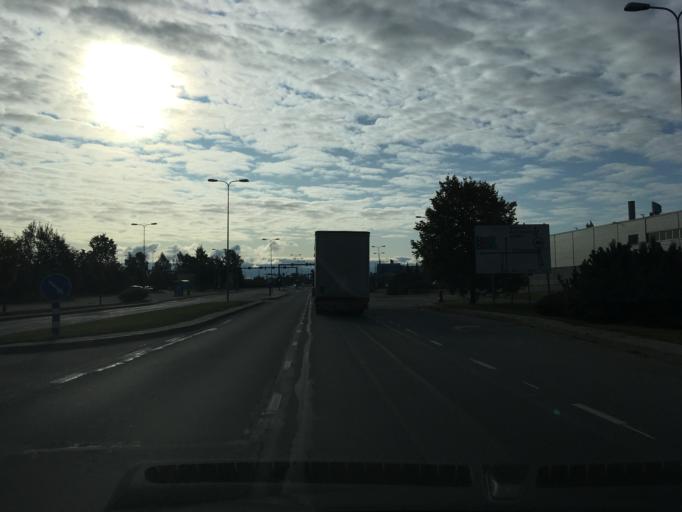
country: EE
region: Harju
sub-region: Tallinna linn
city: Kose
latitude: 59.4314
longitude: 24.8333
